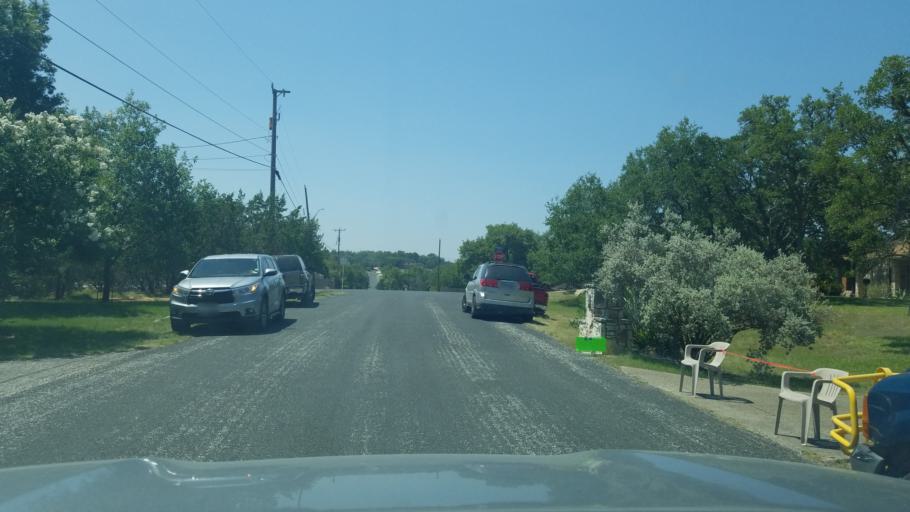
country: US
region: Texas
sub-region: Bexar County
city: Timberwood Park
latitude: 29.7003
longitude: -98.4858
